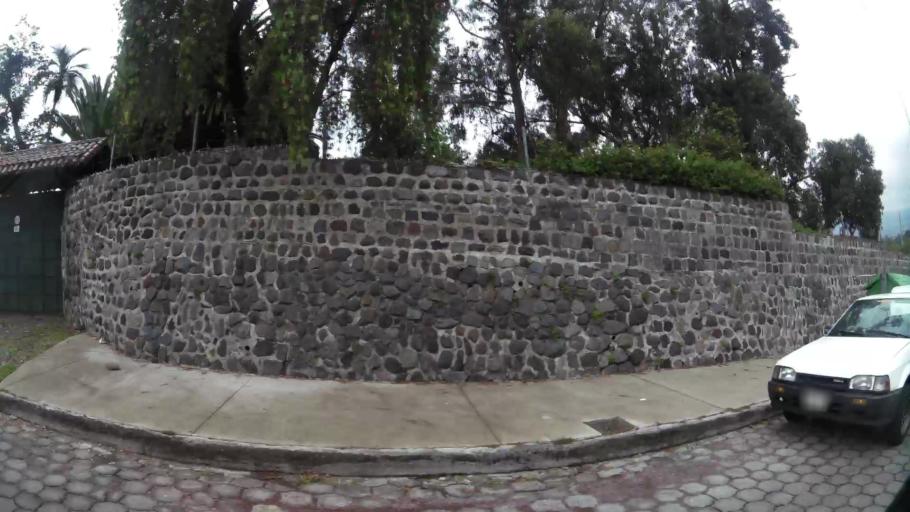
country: EC
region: Pichincha
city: Sangolqui
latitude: -0.3031
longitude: -78.4618
